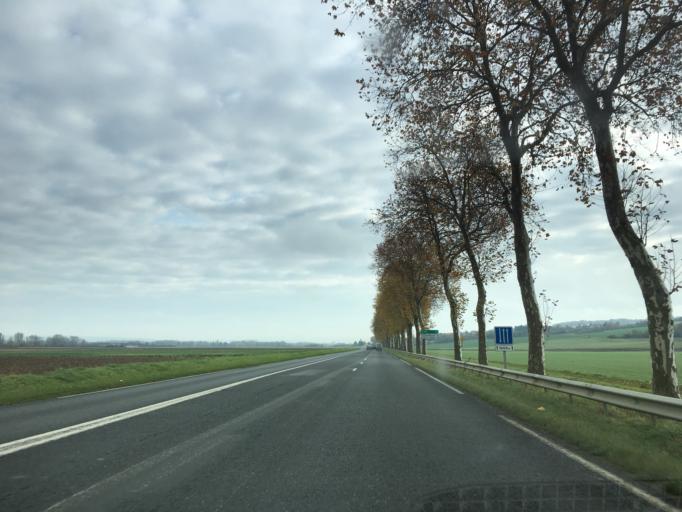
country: FR
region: Bourgogne
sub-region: Departement de l'Yonne
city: Champigny
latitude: 48.3096
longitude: 3.1617
